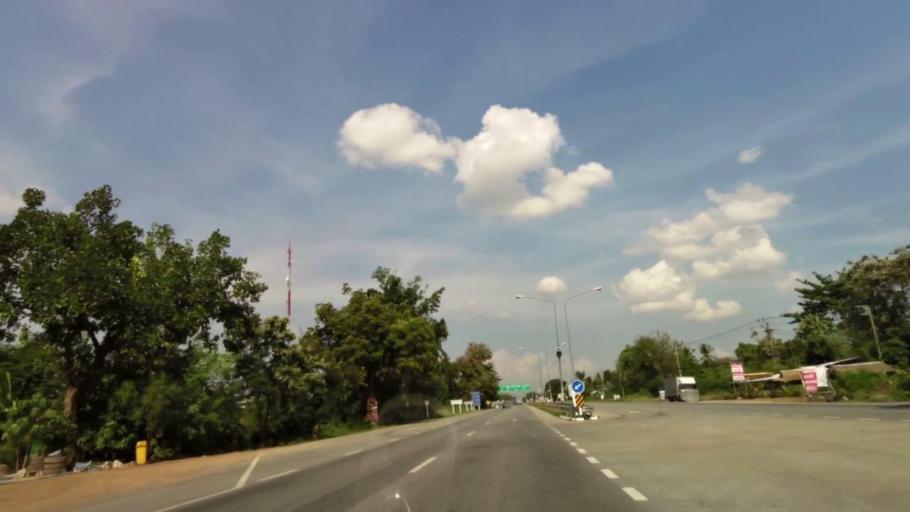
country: TH
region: Uttaradit
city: Thong Saen Khan
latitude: 17.4676
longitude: 100.2367
